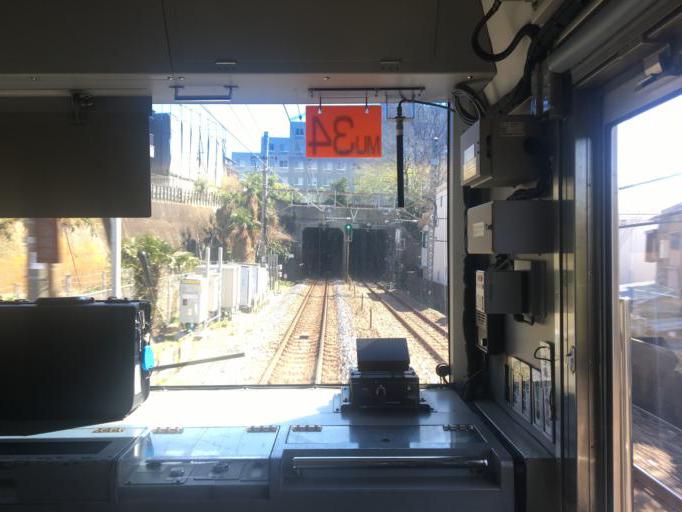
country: JP
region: Saitama
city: Yono
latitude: 35.8456
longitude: 139.6551
